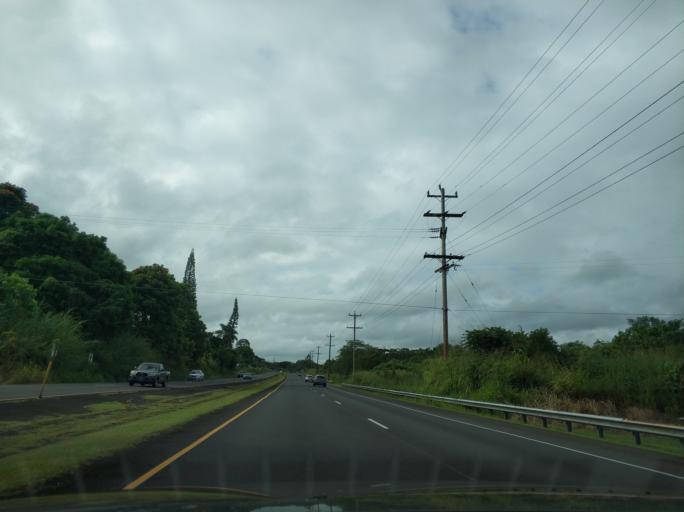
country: US
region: Hawaii
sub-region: Hawaii County
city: Kea'au
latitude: 19.6205
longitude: -155.0425
